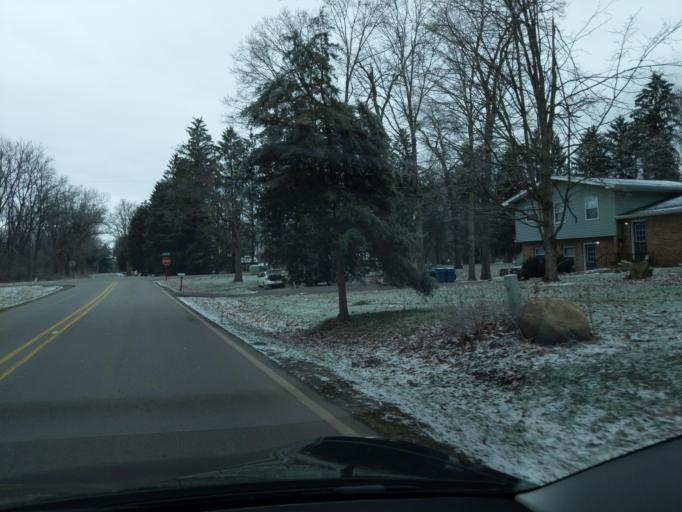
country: US
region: Michigan
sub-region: Jackson County
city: Spring Arbor
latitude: 42.2324
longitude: -84.5170
